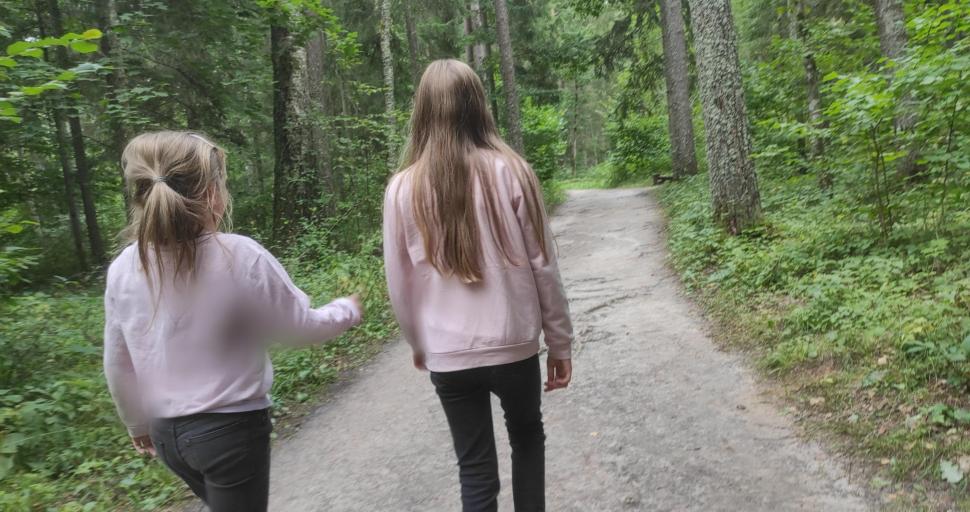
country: LV
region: Kuldigas Rajons
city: Kuldiga
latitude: 57.0072
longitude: 21.9832
